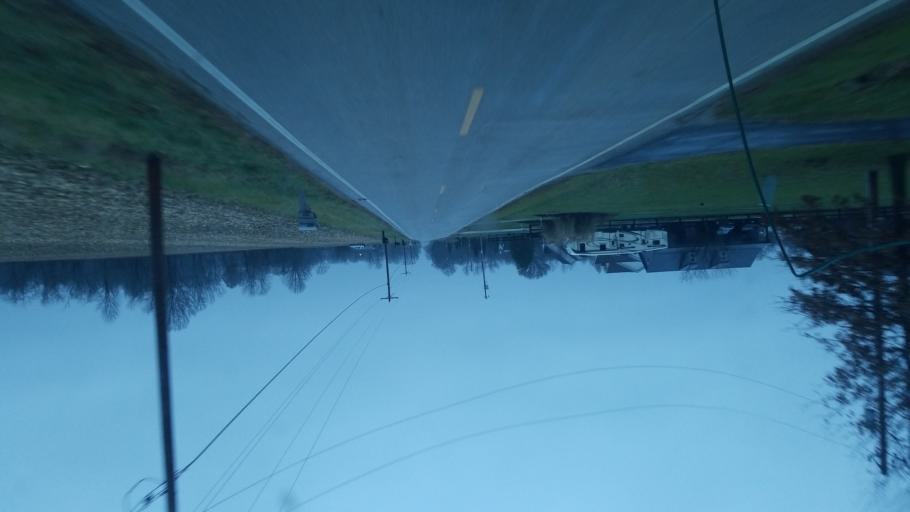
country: US
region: Ohio
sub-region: Delaware County
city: Ashley
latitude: 40.3254
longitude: -82.9322
